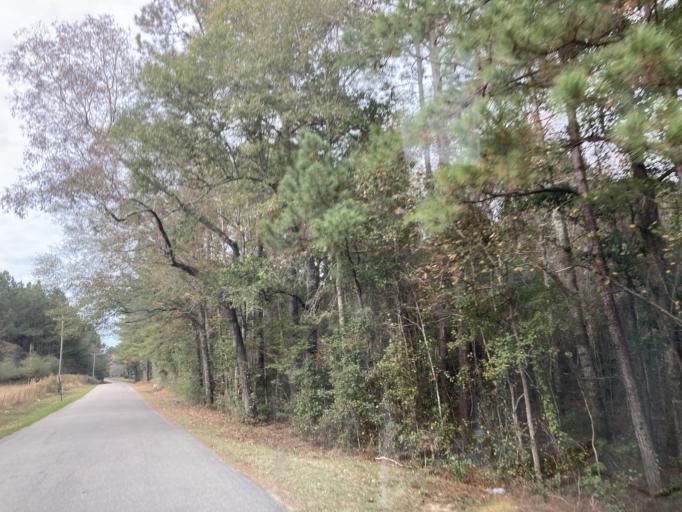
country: US
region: Mississippi
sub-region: Lamar County
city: Purvis
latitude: 31.2405
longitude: -89.4448
